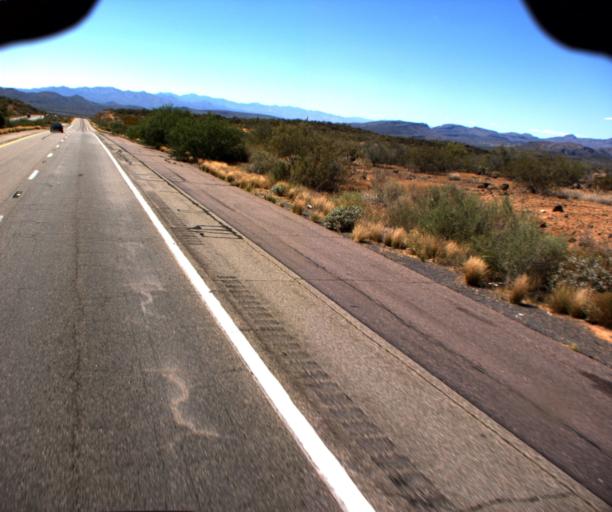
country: US
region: Arizona
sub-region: Yavapai County
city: Bagdad
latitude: 34.4898
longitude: -113.3815
